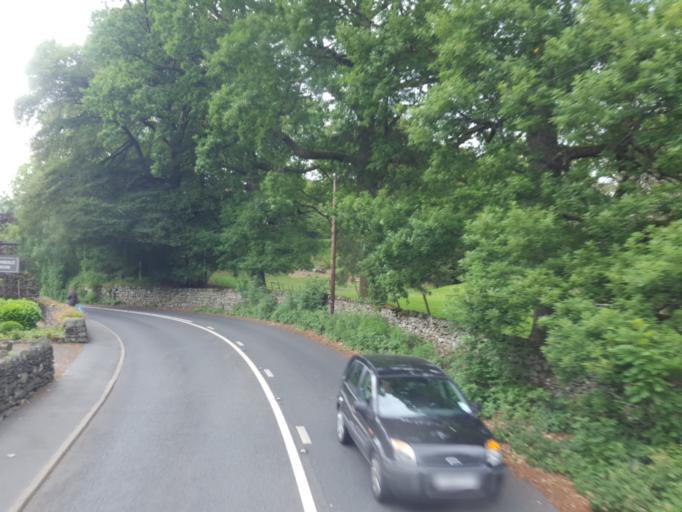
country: GB
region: England
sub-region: Cumbria
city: Ambleside
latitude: 54.4384
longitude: -2.9705
